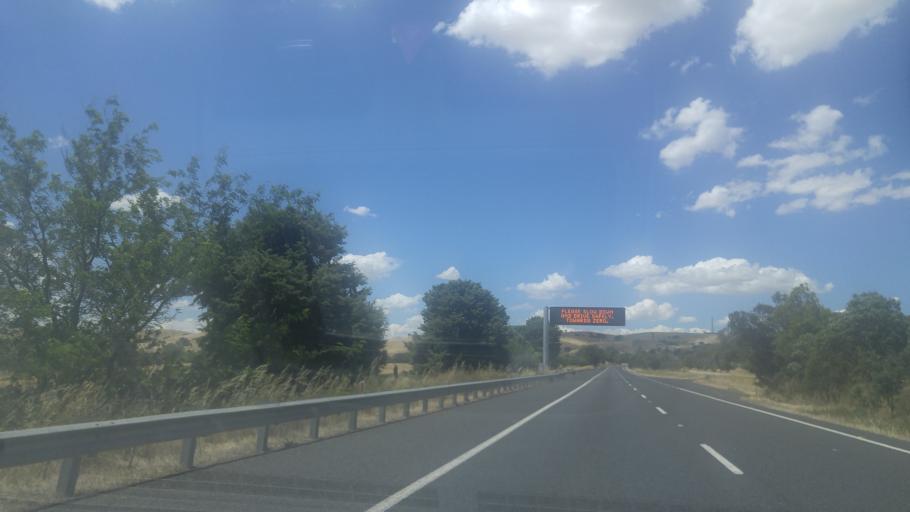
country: AU
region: New South Wales
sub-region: Yass Valley
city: Yass
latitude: -34.7849
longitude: 148.7049
